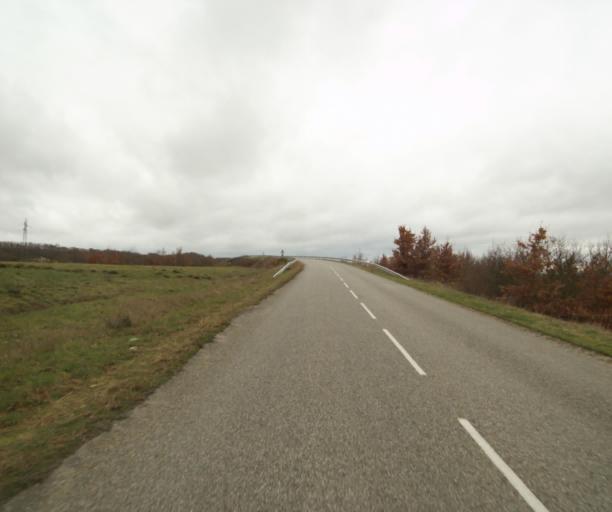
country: FR
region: Midi-Pyrenees
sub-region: Departement de l'Ariege
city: Saverdun
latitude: 43.1998
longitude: 1.6299
